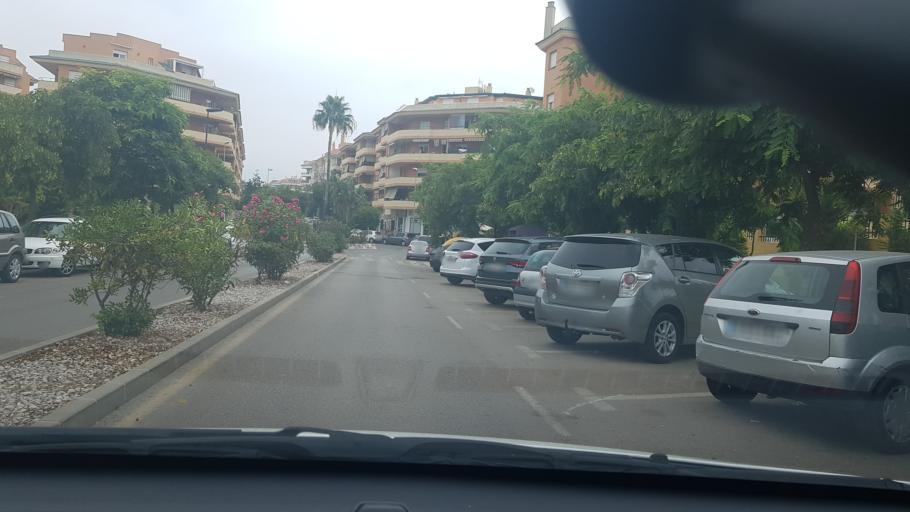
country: ES
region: Andalusia
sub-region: Provincia de Malaga
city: Manilva
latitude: 36.3634
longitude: -5.2306
